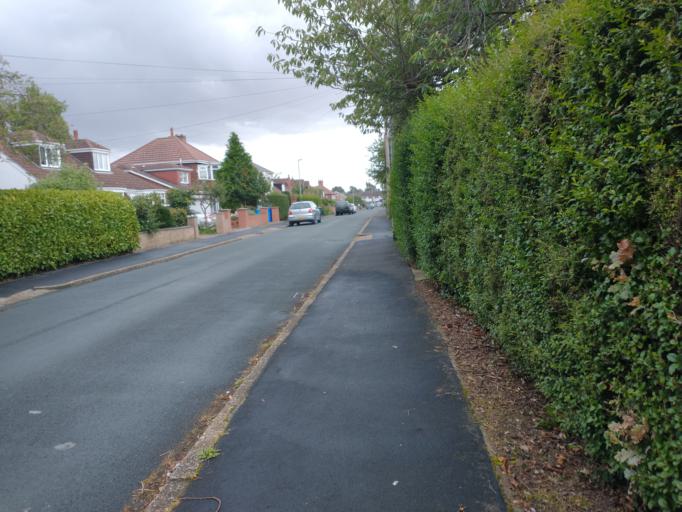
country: GB
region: England
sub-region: East Riding of Yorkshire
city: Willerby
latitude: 53.7583
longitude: -0.4366
